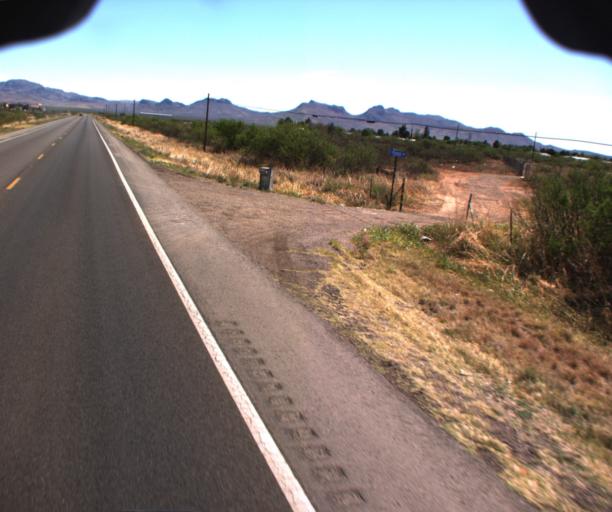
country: US
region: Arizona
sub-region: Cochise County
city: Douglas
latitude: 31.3701
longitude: -109.5321
